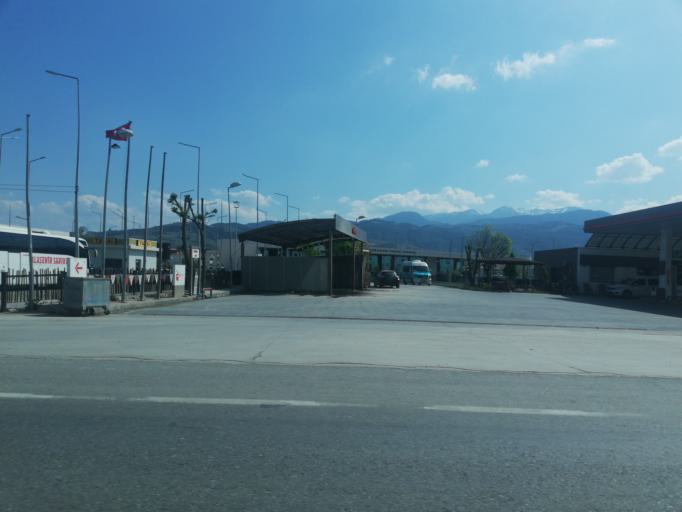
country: TR
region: Manisa
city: Alasehir
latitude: 38.3591
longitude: 28.5385
